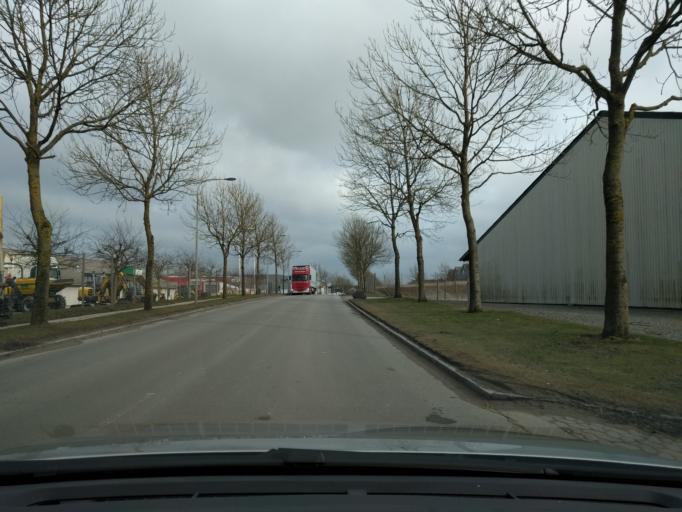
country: DK
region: South Denmark
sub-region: Odense Kommune
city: Bellinge
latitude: 55.3580
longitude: 10.3316
